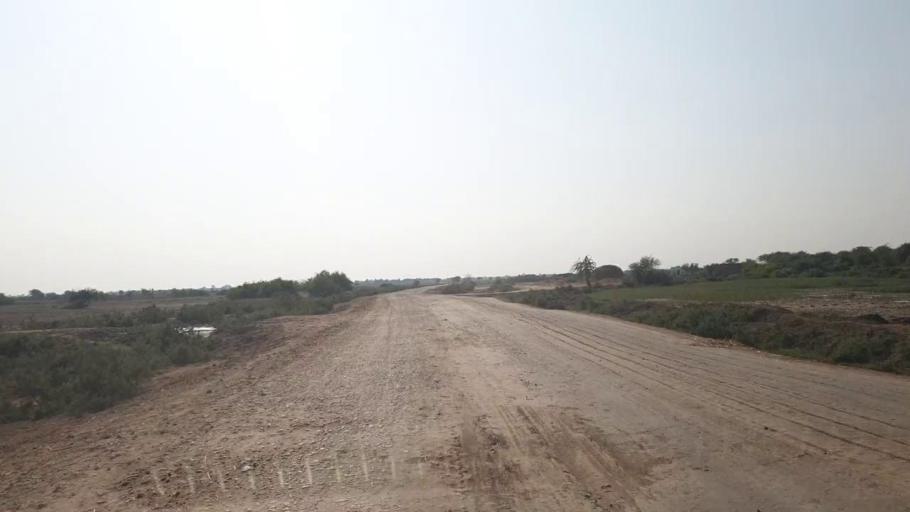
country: PK
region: Sindh
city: Matli
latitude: 24.9343
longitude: 68.6679
